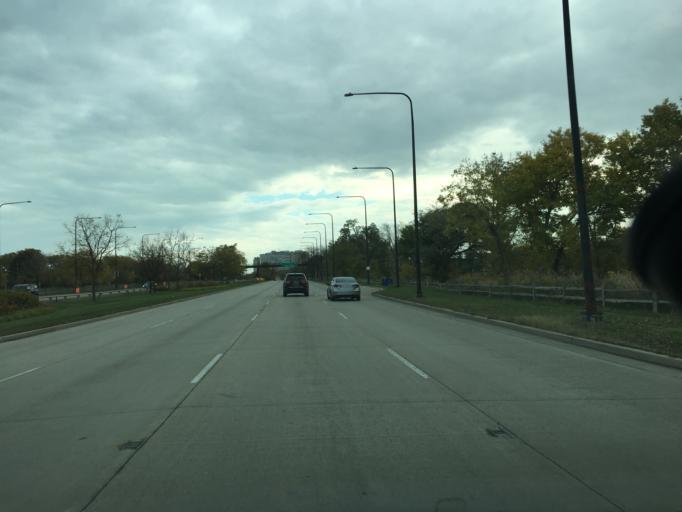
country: US
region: Illinois
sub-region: Cook County
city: Chicago
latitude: 41.8193
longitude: -87.5971
